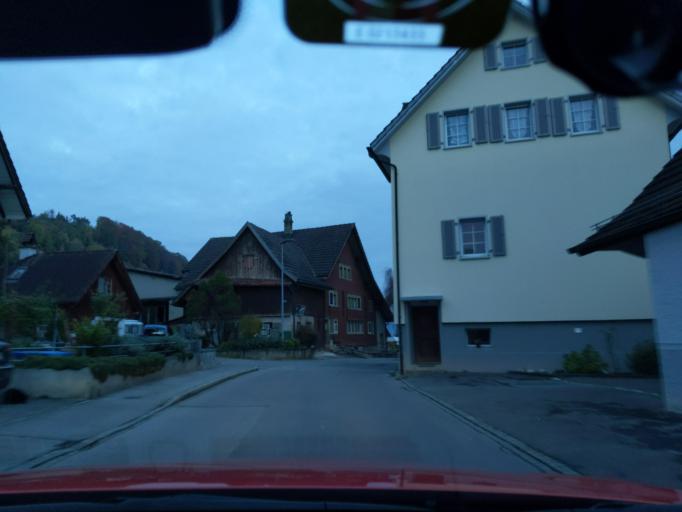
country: CH
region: Saint Gallen
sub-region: Wahlkreis Rheintal
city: Au
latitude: 47.4275
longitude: 9.6125
